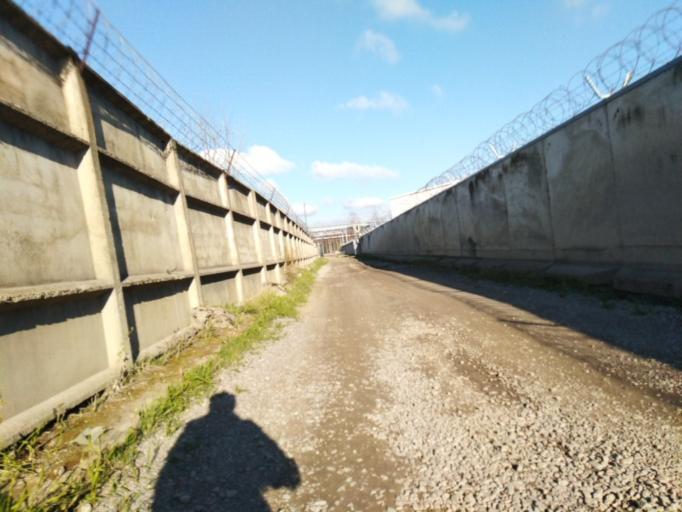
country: RU
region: Leningrad
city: Novoye Devyatkino
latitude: 60.0722
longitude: 30.4756
